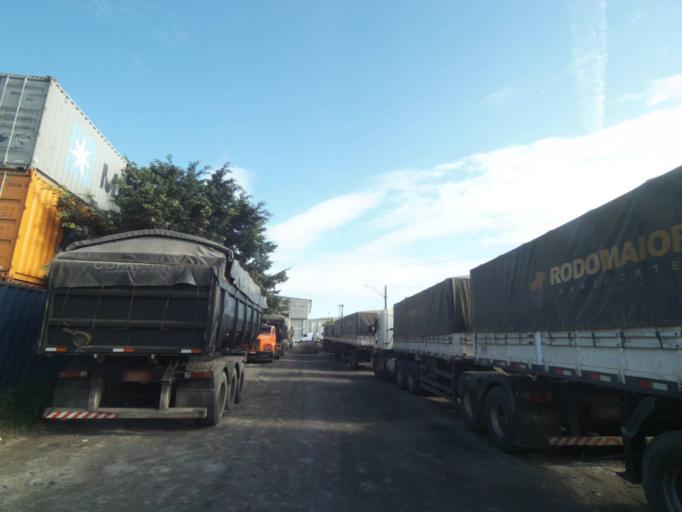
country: BR
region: Parana
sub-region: Paranagua
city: Paranagua
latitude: -25.5130
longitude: -48.5223
